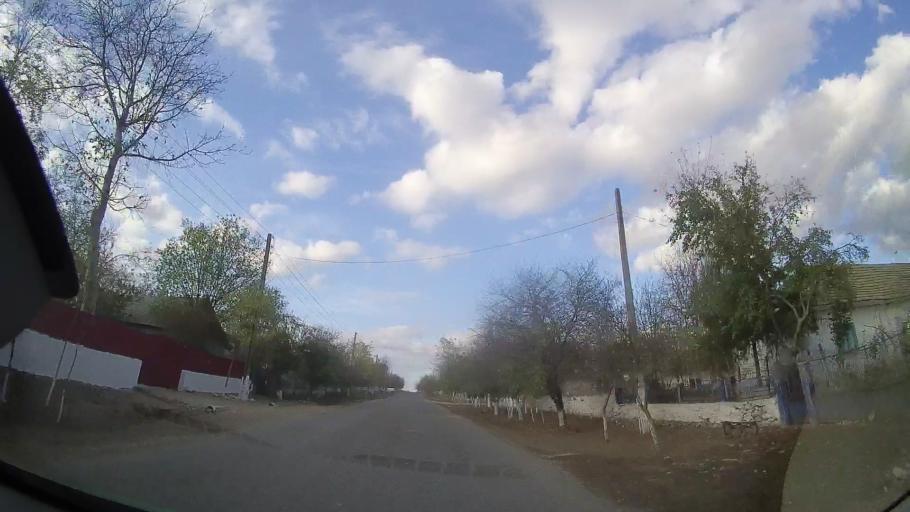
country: RO
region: Constanta
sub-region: Comuna Cerchezu
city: Cerchezu
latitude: 43.8612
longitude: 28.1012
